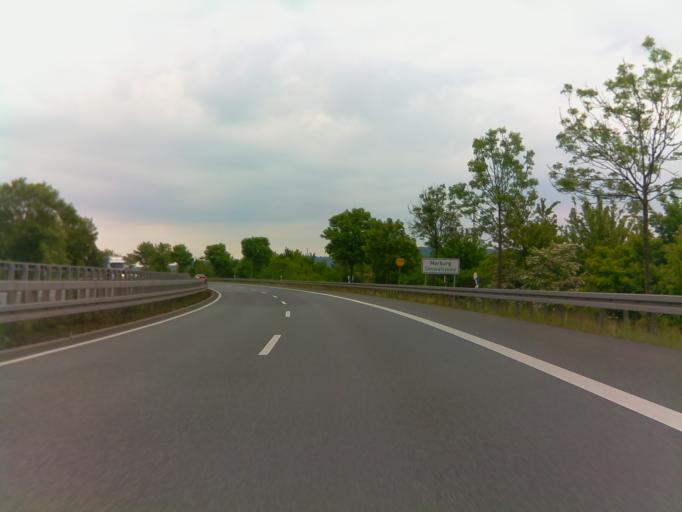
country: DE
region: Hesse
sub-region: Regierungsbezirk Giessen
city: Marburg an der Lahn
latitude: 50.7752
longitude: 8.7596
